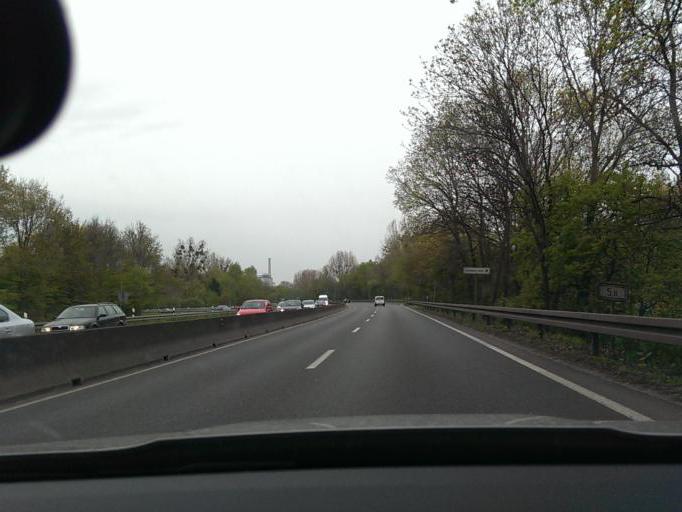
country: DE
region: Lower Saxony
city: Hannover
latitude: 52.3858
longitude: 9.6902
